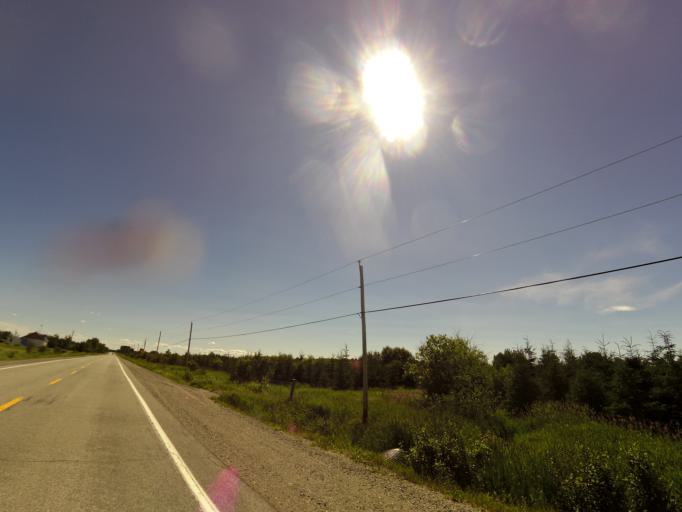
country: CA
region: Quebec
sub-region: Abitibi-Temiscamingue
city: Senneterre
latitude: 48.2684
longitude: -77.3229
